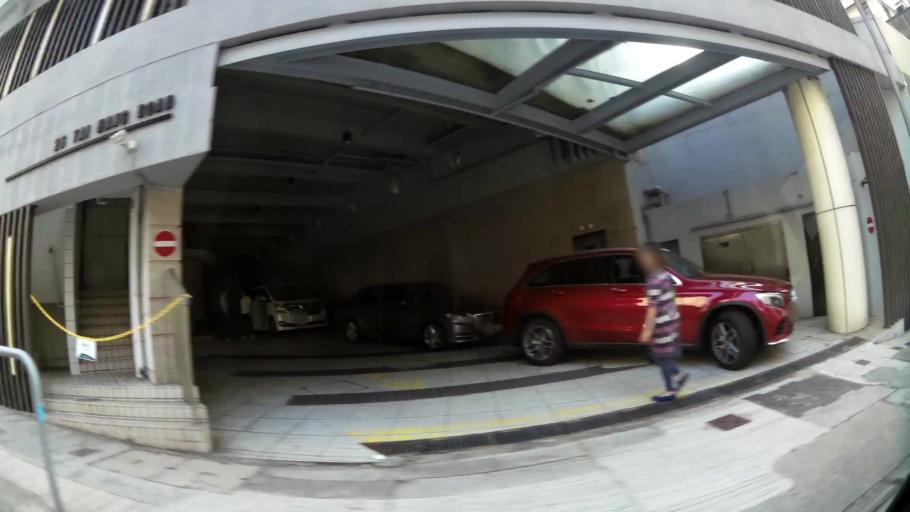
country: HK
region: Wanchai
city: Wan Chai
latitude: 22.2770
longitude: 114.1936
